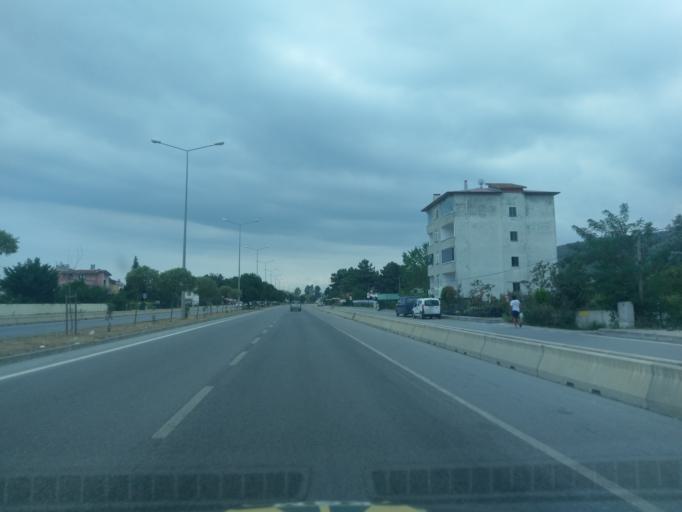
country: TR
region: Samsun
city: Taflan
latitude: 41.3976
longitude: 36.1954
